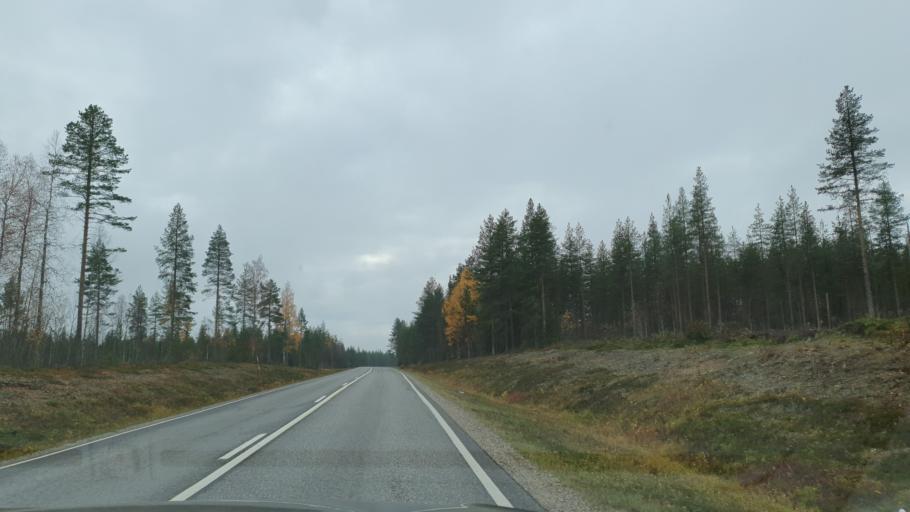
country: FI
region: Lapland
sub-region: Rovaniemi
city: Ranua
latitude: 66.0377
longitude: 26.3383
